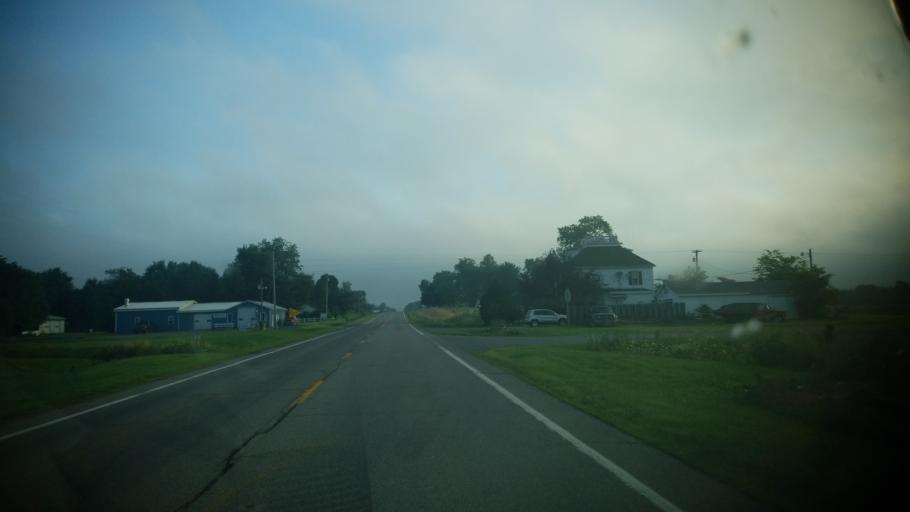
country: US
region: Illinois
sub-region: Wayne County
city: Fairfield
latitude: 38.3831
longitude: -88.4057
